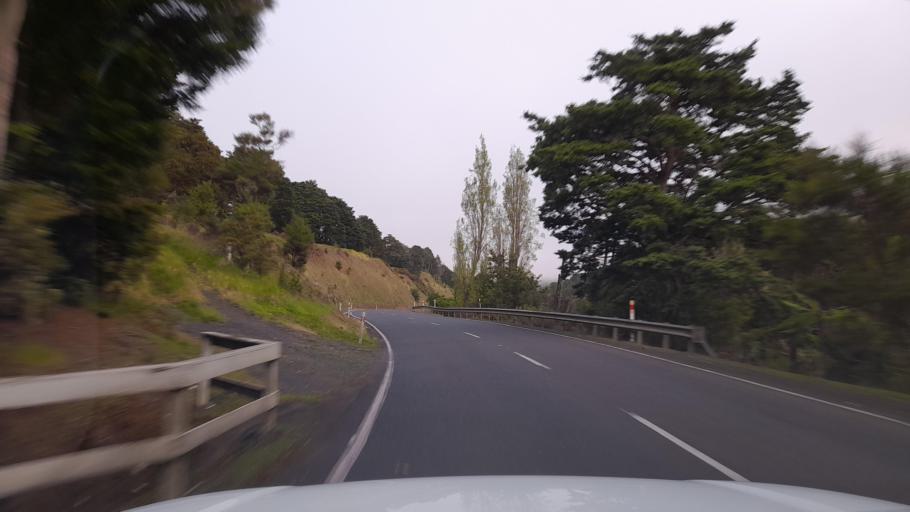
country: NZ
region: Northland
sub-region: Kaipara District
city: Dargaville
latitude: -35.6298
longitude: 173.8532
